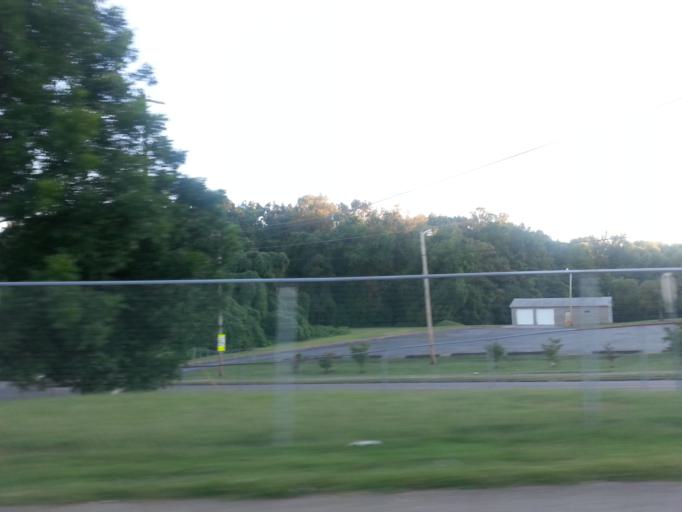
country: US
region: Tennessee
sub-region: Knox County
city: Knoxville
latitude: 35.9724
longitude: -83.8924
